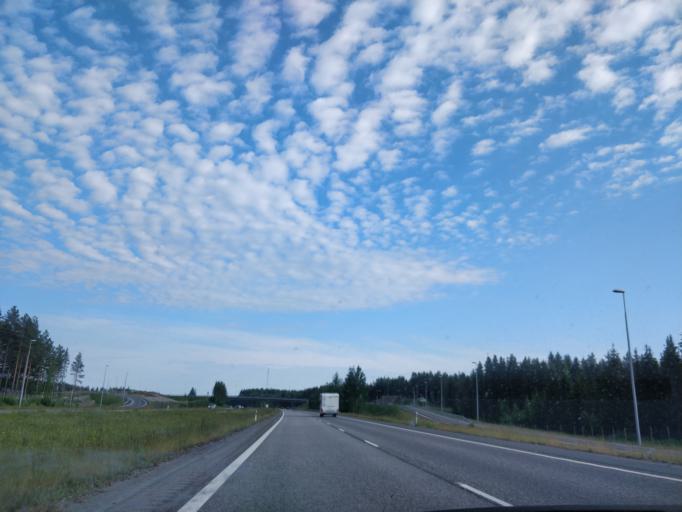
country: FI
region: Haeme
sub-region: Riihimaeki
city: Riihimaeki
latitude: 60.6915
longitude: 24.7463
